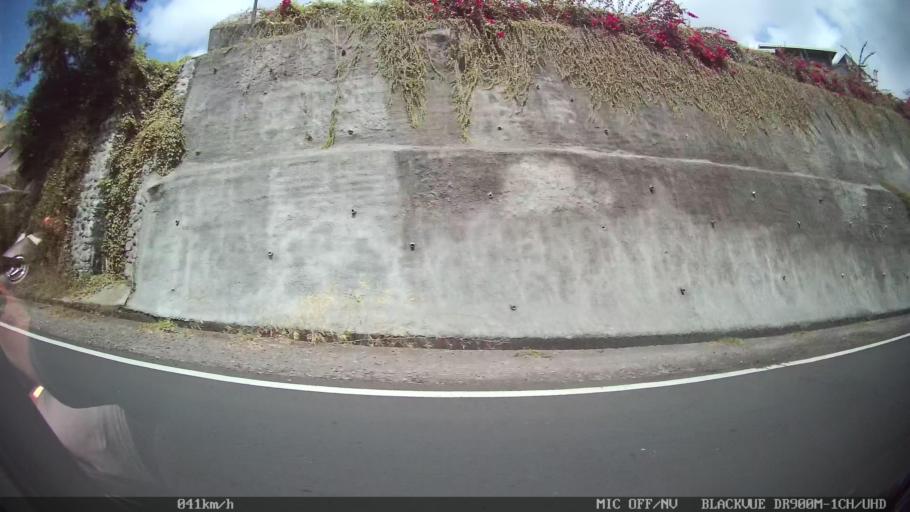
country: ID
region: Bali
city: Banjar Pasekan
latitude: -8.5888
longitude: 115.2879
